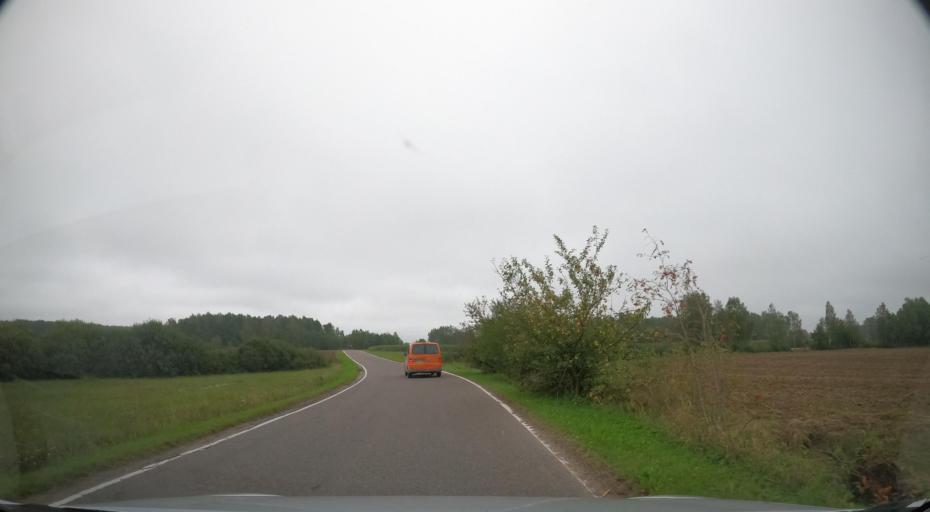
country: PL
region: Pomeranian Voivodeship
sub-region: Powiat wejherowski
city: Szemud
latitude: 54.5022
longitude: 18.1651
